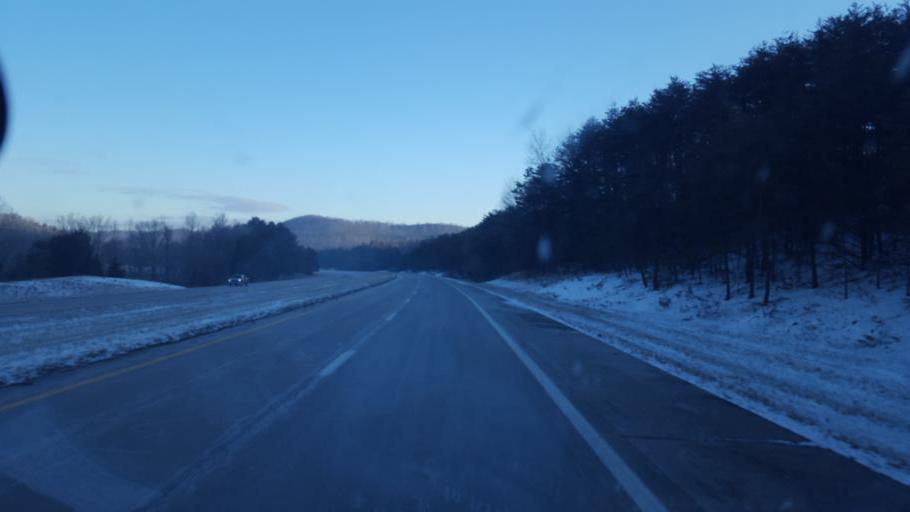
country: US
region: Ohio
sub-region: Adams County
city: Peebles
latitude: 38.9978
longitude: -83.3008
